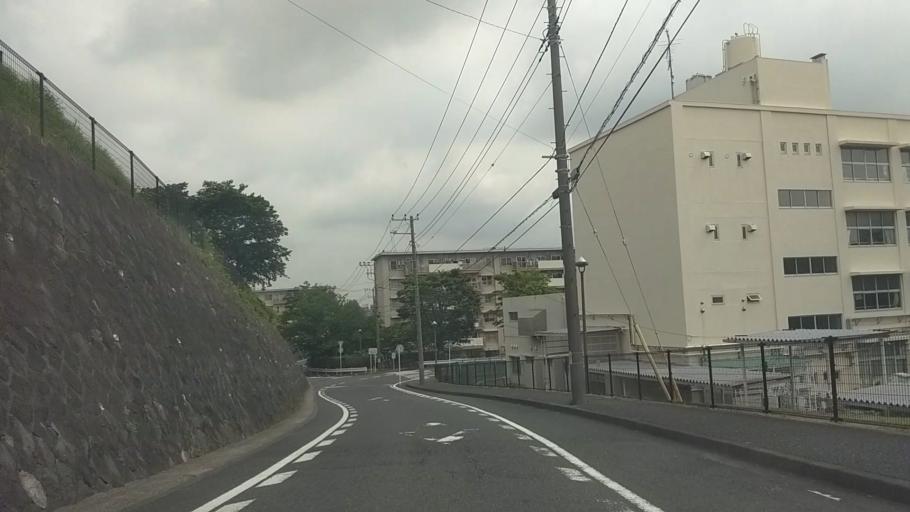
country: JP
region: Kanagawa
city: Kamakura
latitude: 35.3726
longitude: 139.5343
